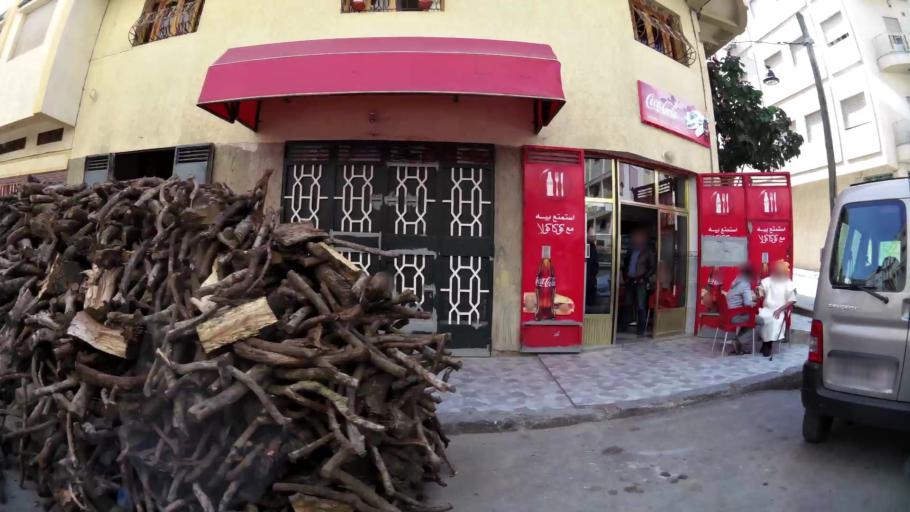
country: MA
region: Tanger-Tetouan
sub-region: Tanger-Assilah
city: Tangier
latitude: 35.7615
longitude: -5.8371
